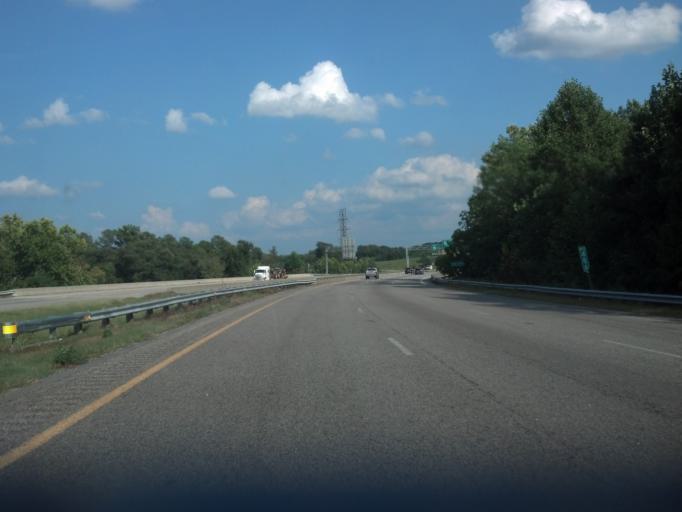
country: US
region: North Carolina
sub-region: Edgecombe County
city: Princeville
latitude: 35.8880
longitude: -77.5407
